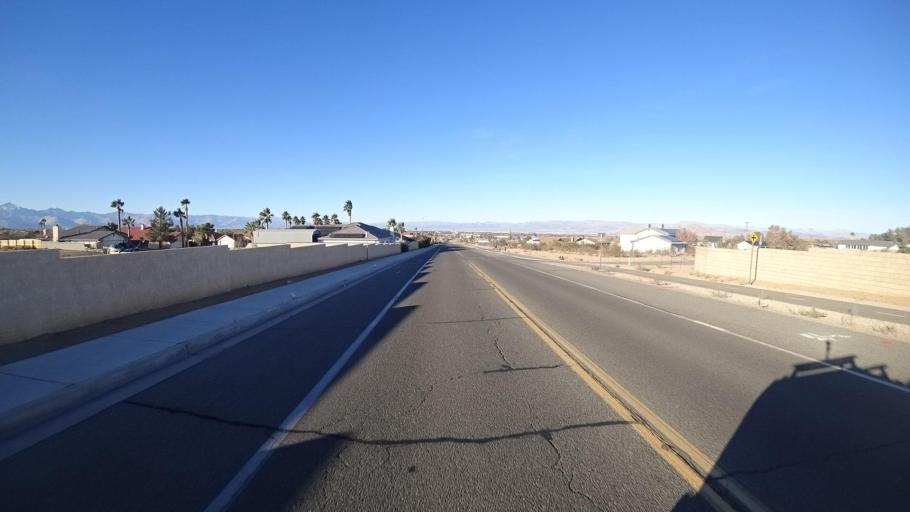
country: US
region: California
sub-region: Kern County
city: Ridgecrest
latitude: 35.5841
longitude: -117.6703
